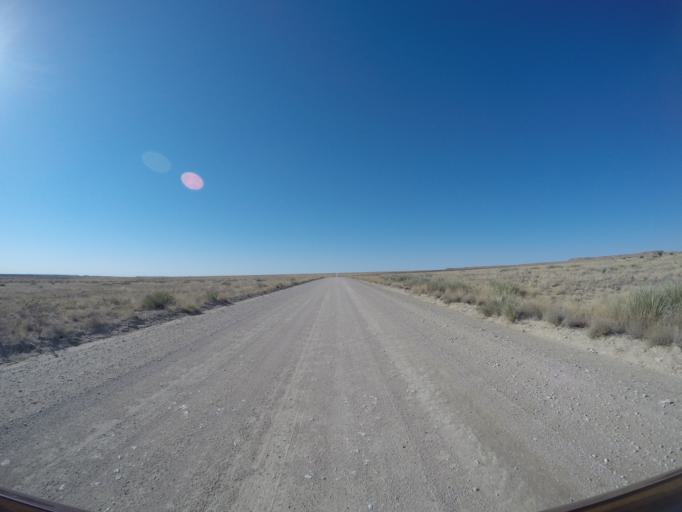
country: US
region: Colorado
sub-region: Otero County
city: La Junta
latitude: 37.7971
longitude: -103.5090
